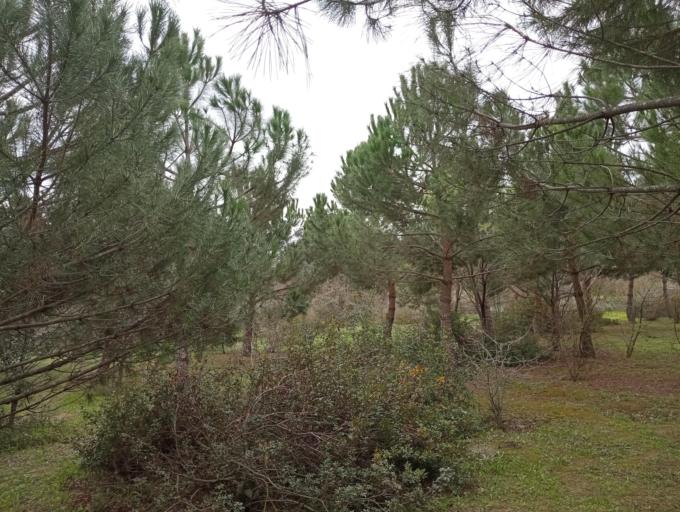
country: ES
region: Madrid
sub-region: Provincia de Madrid
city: Latina
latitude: 40.4020
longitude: -3.7740
